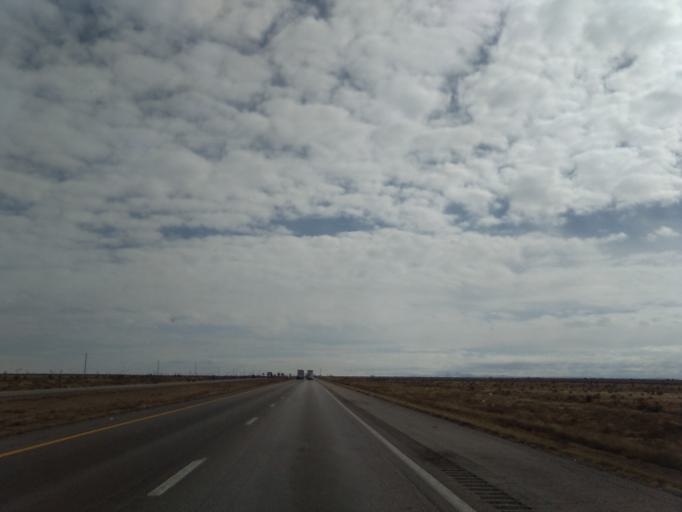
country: US
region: New Mexico
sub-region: Hidalgo County
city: Lordsburg
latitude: 32.2252
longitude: -108.4617
